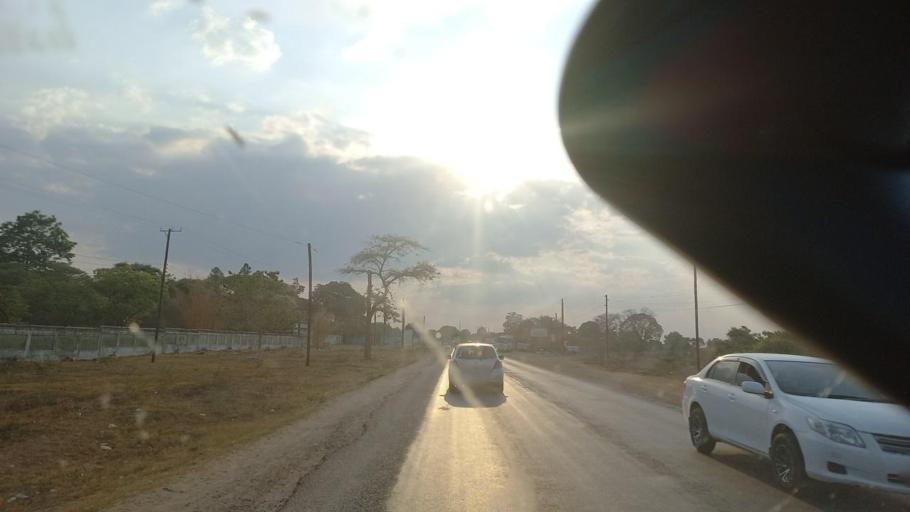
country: ZM
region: Lusaka
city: Lusaka
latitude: -15.3681
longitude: 28.4133
